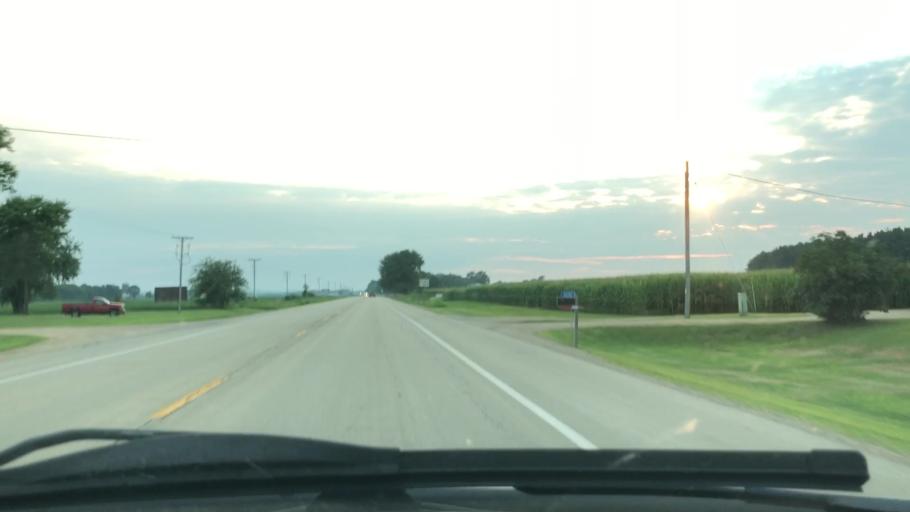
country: US
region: Wisconsin
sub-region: Sauk County
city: Spring Green
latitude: 43.1898
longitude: -90.0809
